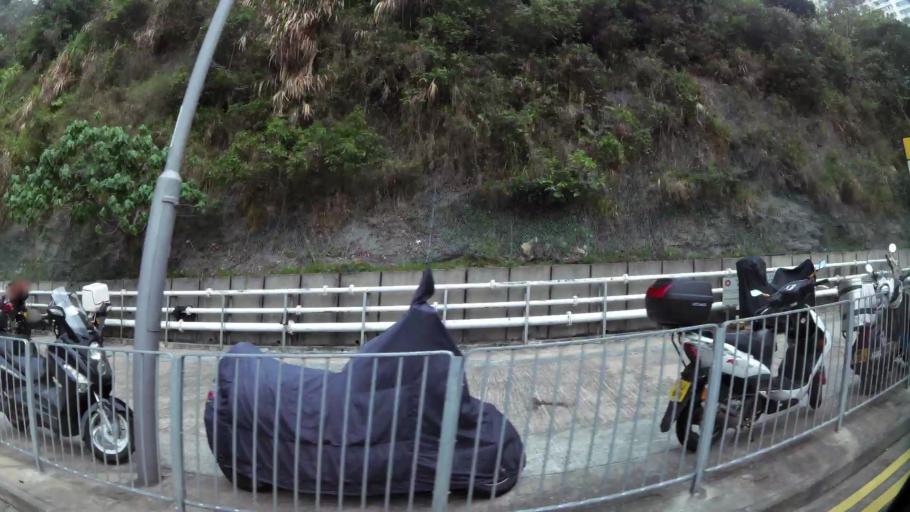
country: HK
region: Wanchai
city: Wan Chai
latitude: 22.2621
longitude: 114.2324
